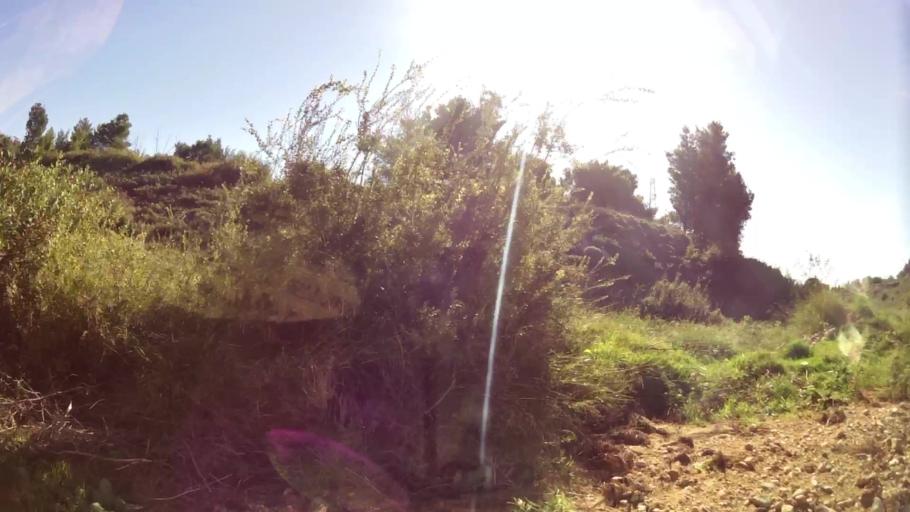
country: GR
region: Attica
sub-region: Nomarchia Anatolikis Attikis
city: Varybobi
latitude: 38.1248
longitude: 23.7773
